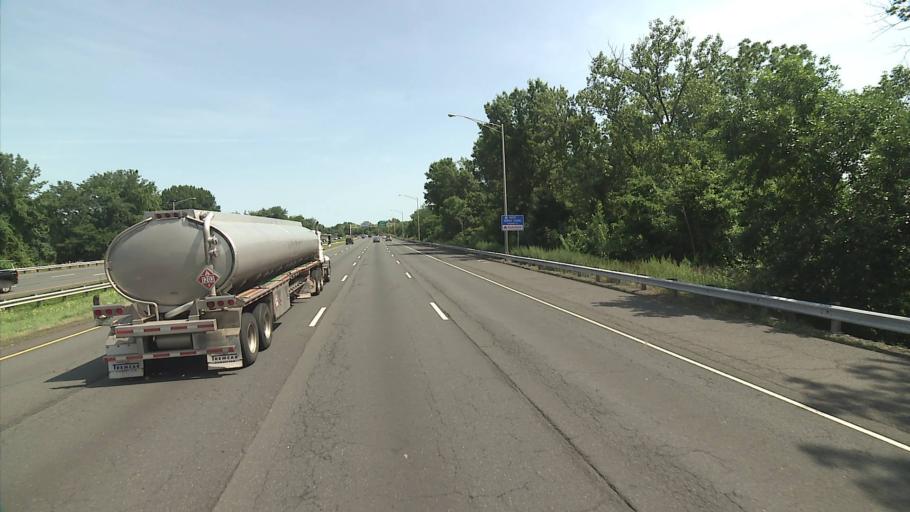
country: US
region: Connecticut
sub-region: Hartford County
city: Wethersfield
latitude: 41.6940
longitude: -72.6460
